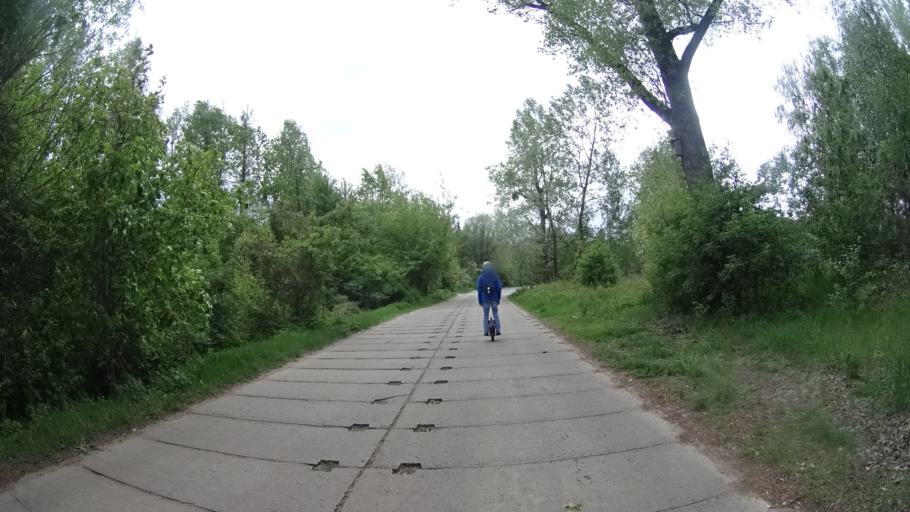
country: PL
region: Masovian Voivodeship
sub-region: Warszawa
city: Bemowo
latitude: 52.2811
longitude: 20.8859
